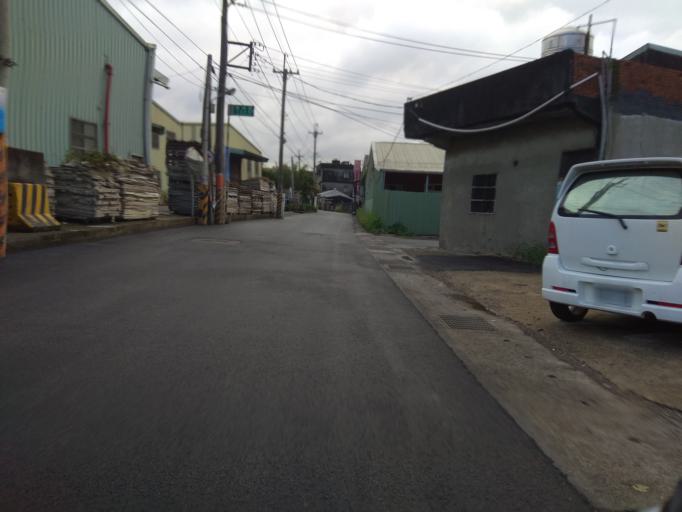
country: TW
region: Taiwan
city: Daxi
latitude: 24.9401
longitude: 121.1896
